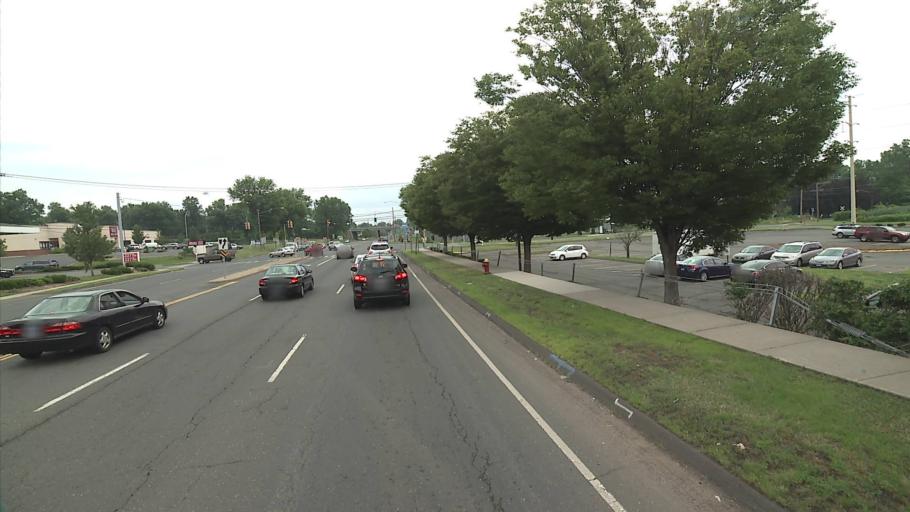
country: US
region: Connecticut
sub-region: Hartford County
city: Wethersfield
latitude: 41.7231
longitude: -72.6680
